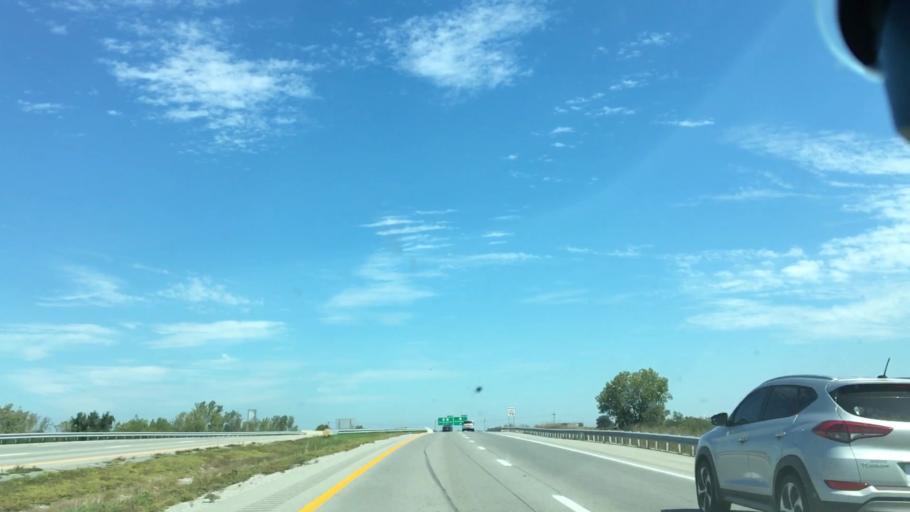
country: US
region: Kentucky
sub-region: Christian County
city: Hopkinsville
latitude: 36.8386
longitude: -87.4684
